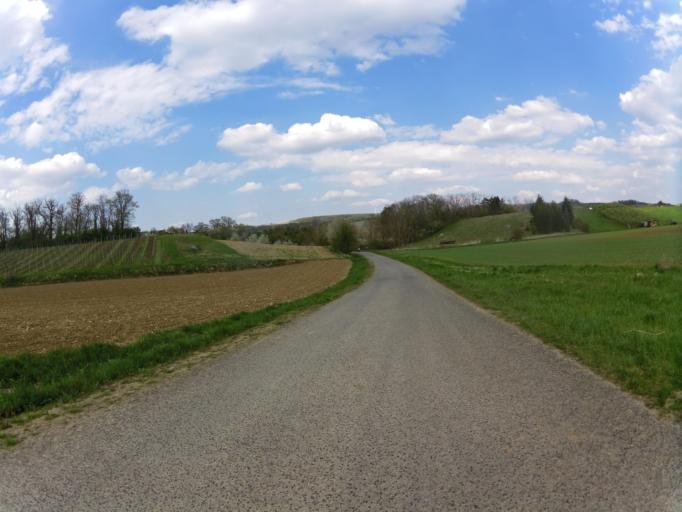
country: DE
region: Bavaria
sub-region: Regierungsbezirk Unterfranken
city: Winterhausen
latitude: 49.7004
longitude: 10.0137
